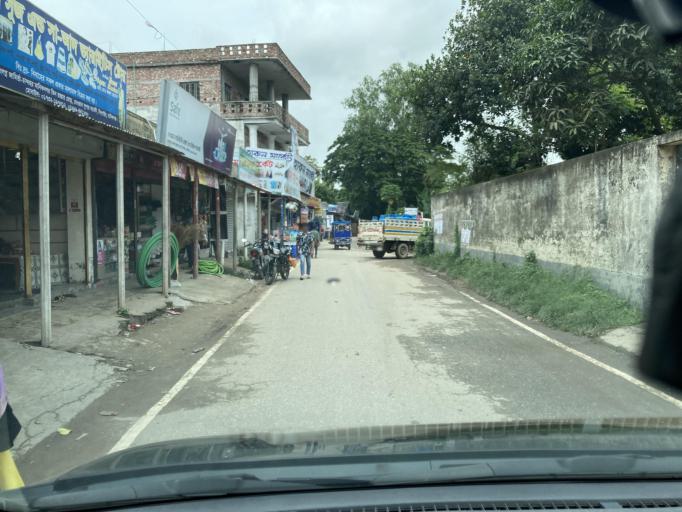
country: BD
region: Dhaka
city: Dohar
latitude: 23.7611
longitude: 90.2034
